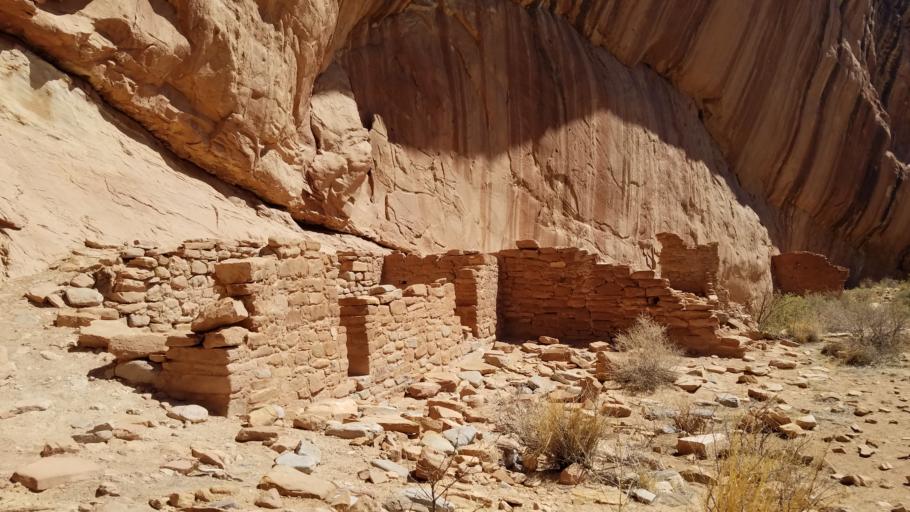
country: US
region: Utah
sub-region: San Juan County
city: Blanding
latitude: 37.5467
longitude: -109.6722
